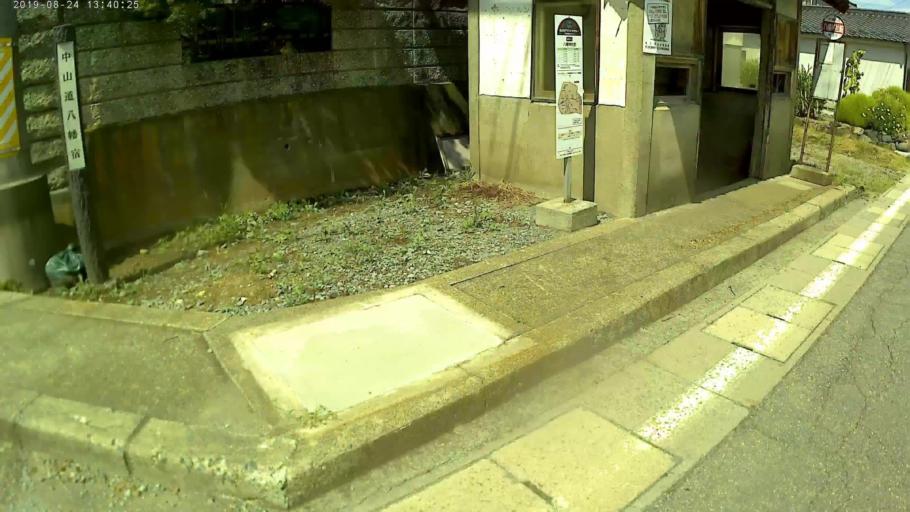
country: JP
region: Nagano
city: Komoro
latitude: 36.2753
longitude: 138.3983
